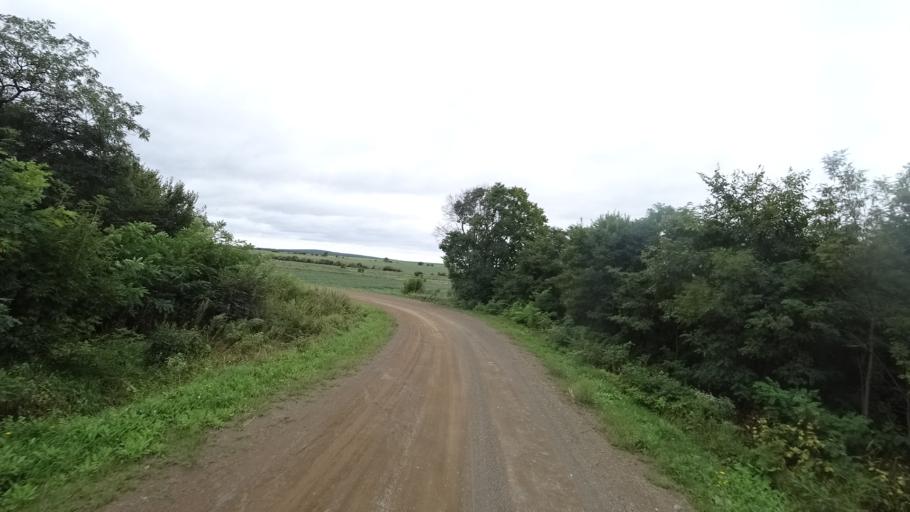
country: RU
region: Primorskiy
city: Chernigovka
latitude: 44.4541
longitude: 132.5834
